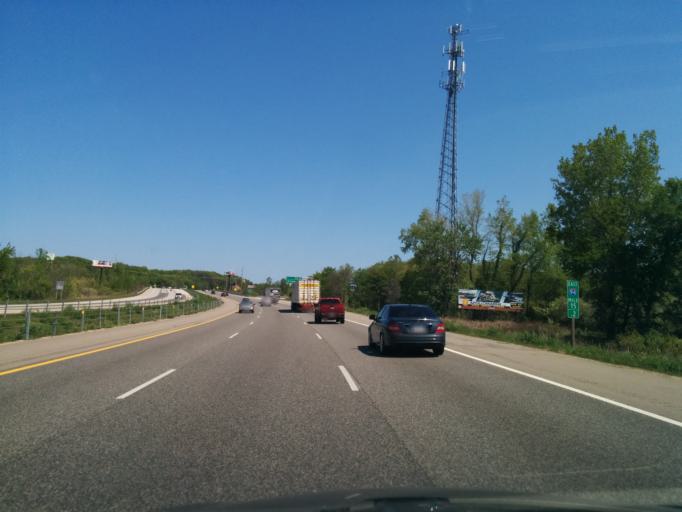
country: US
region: Michigan
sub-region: Berrien County
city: Bridgman
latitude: 41.9252
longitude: -86.5700
